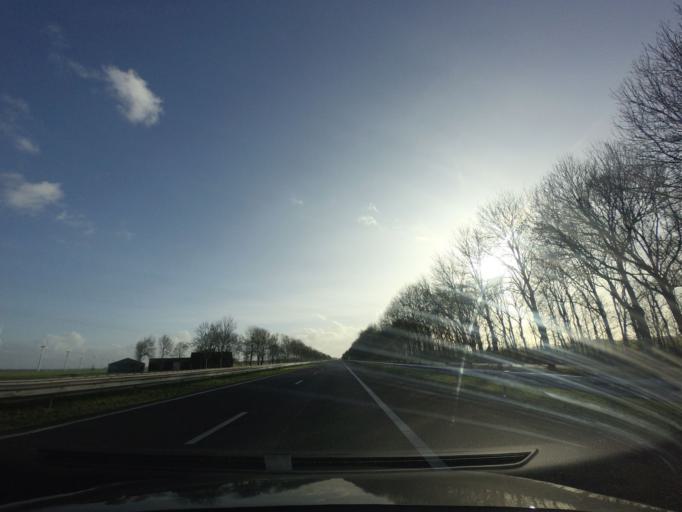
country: NL
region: North Holland
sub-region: Gemeente Hollands Kroon
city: Den Oever
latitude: 52.8903
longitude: 5.0254
